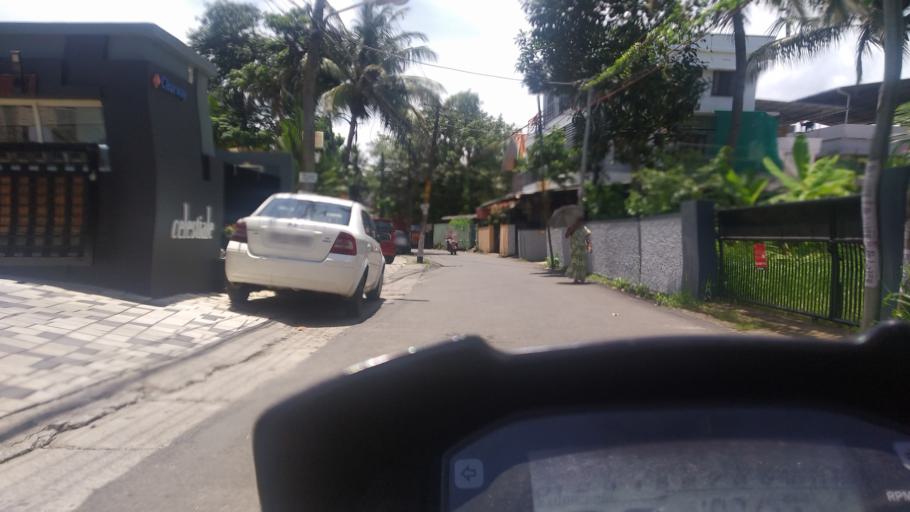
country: IN
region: Kerala
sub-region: Ernakulam
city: Cochin
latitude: 9.9761
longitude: 76.3034
